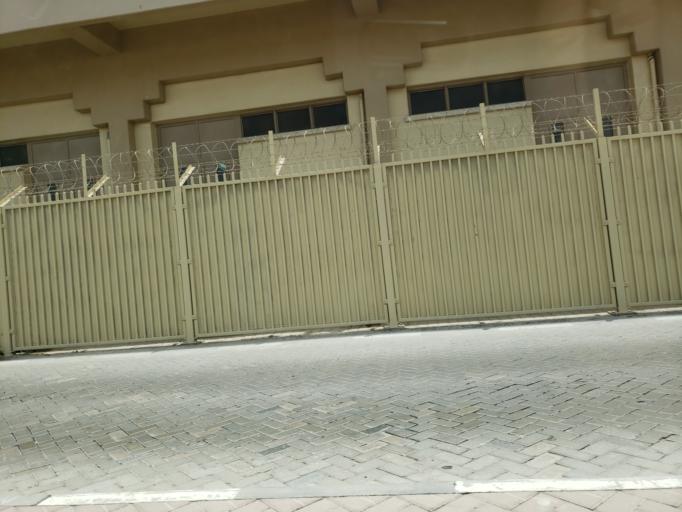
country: AE
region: Ash Shariqah
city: Sharjah
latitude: 25.2225
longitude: 55.2803
